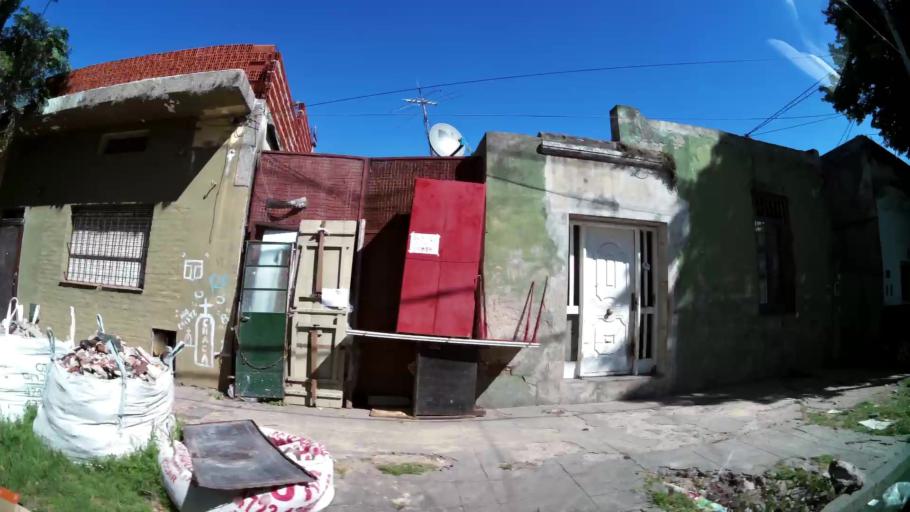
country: AR
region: Buenos Aires
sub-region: Partido de San Isidro
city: San Isidro
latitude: -34.4649
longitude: -58.5331
